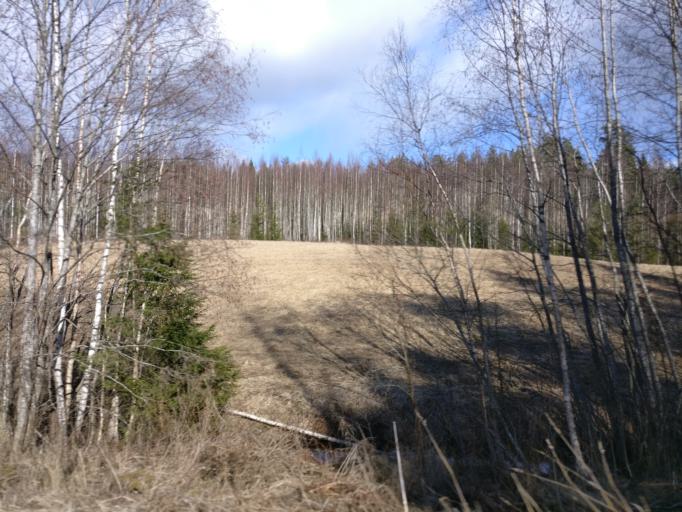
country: FI
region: Uusimaa
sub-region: Helsinki
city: Sammatti
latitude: 60.2860
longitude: 23.7678
